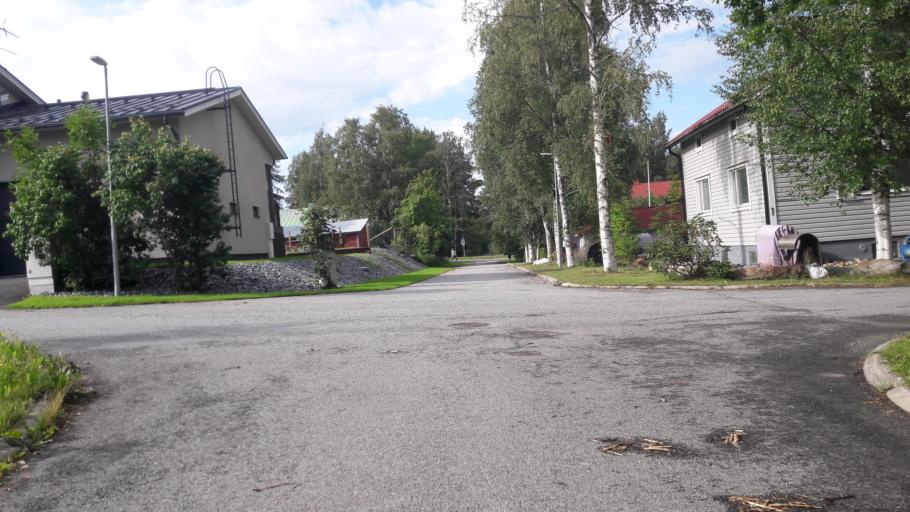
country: FI
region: North Karelia
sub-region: Joensuu
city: Joensuu
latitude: 62.5967
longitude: 29.7908
